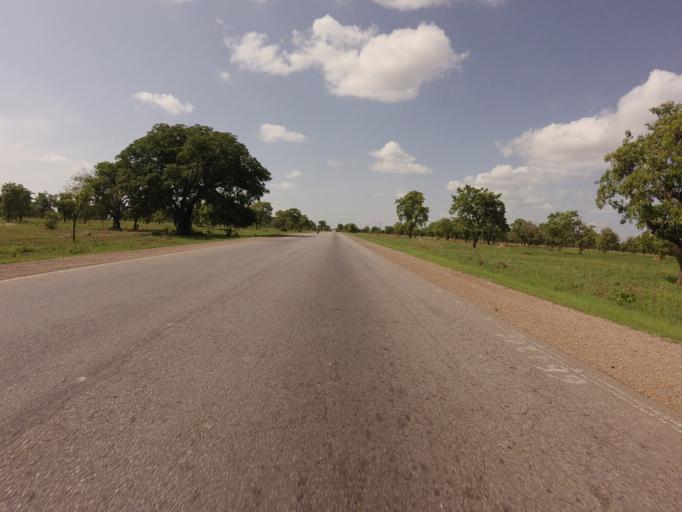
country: GH
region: Northern
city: Savelugu
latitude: 9.9650
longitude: -0.8310
